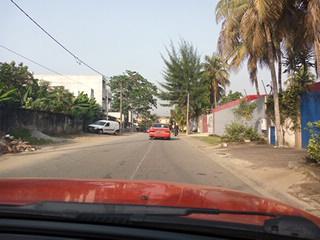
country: CI
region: Lagunes
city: Abobo
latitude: 5.3746
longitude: -3.9895
